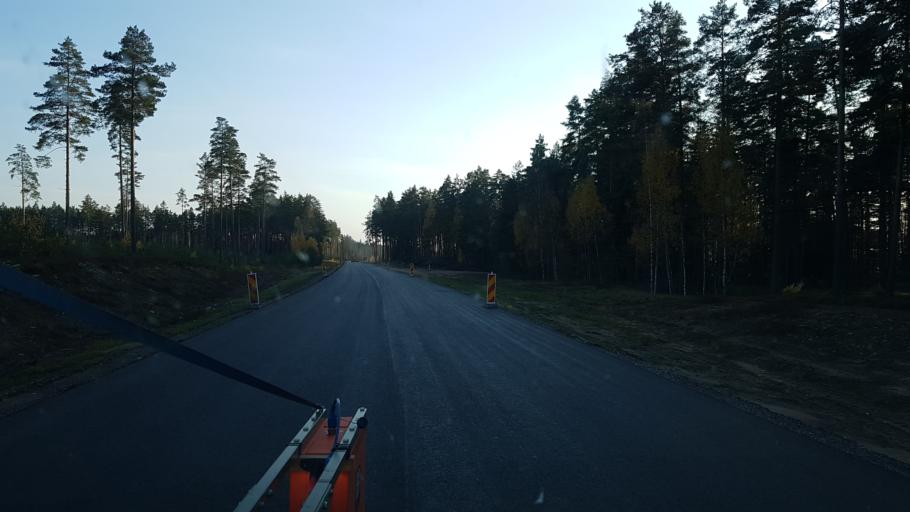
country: EE
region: Polvamaa
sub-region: Polva linn
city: Polva
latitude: 57.9269
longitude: 27.1825
